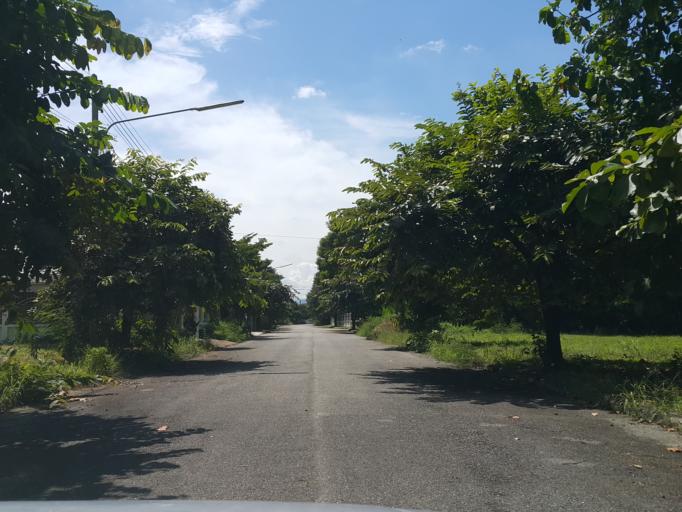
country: TH
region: Chiang Mai
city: Chiang Mai
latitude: 18.7365
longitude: 98.9645
